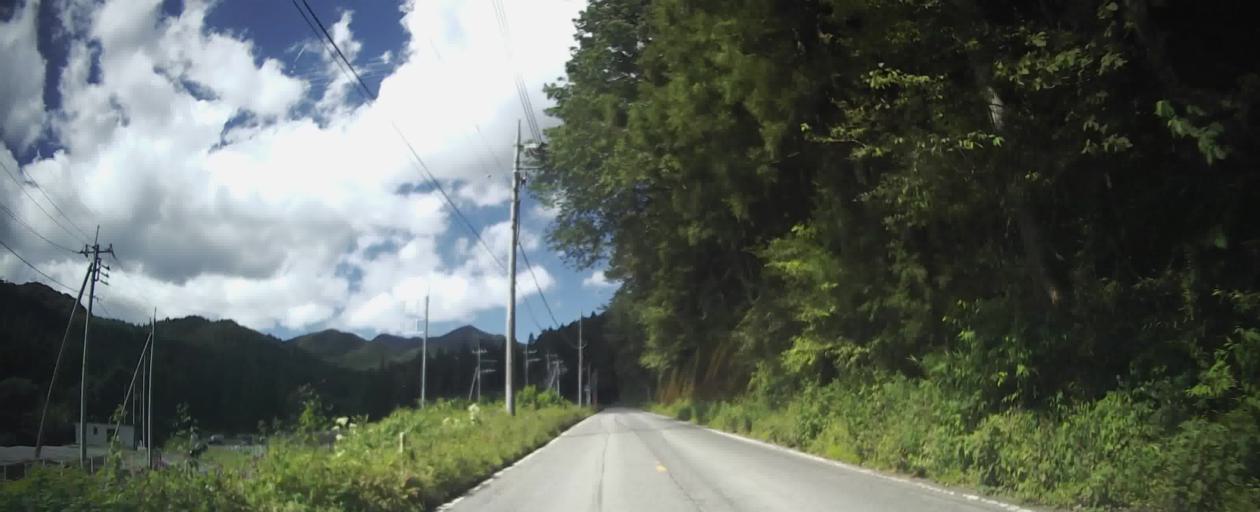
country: JP
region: Gunma
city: Kanekomachi
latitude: 36.4379
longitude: 138.9158
